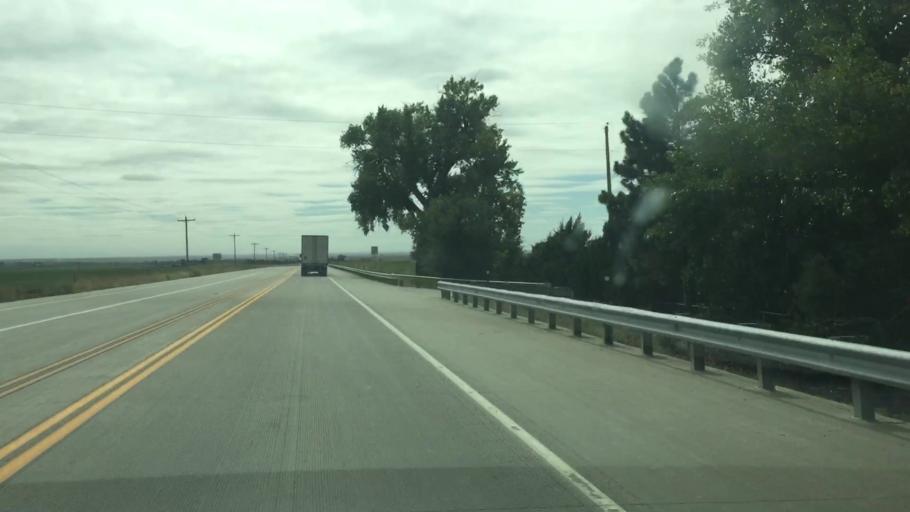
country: US
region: Colorado
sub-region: Prowers County
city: Lamar
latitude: 38.2009
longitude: -102.7242
